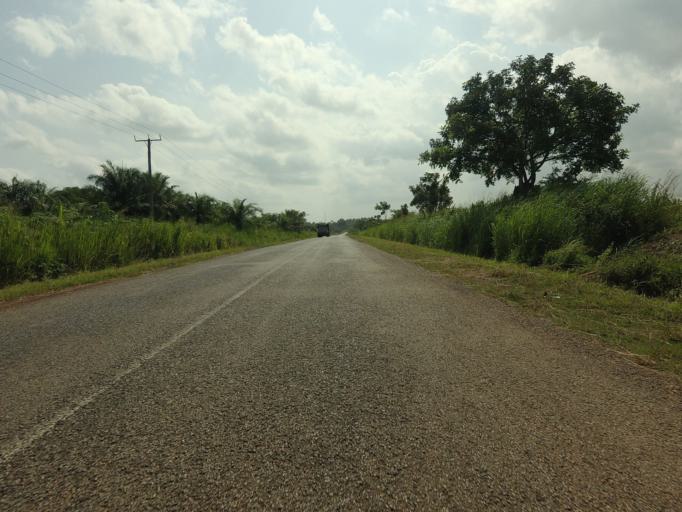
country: GH
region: Volta
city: Ho
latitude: 6.4091
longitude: 0.7665
